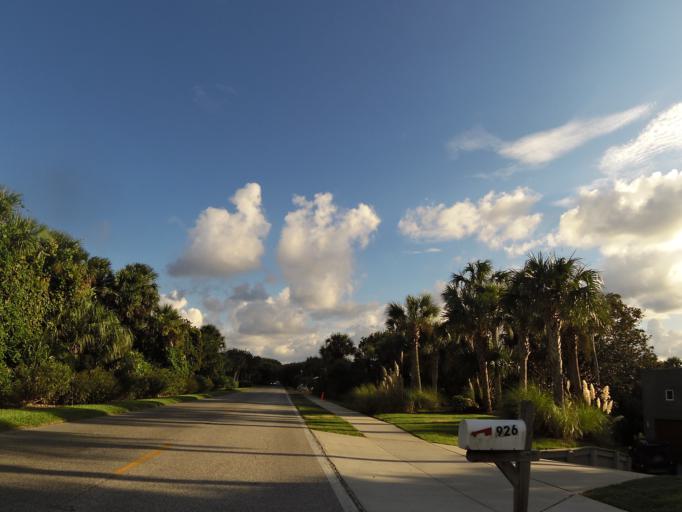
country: US
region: Florida
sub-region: Saint Johns County
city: Sawgrass
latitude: 30.1851
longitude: -81.3632
